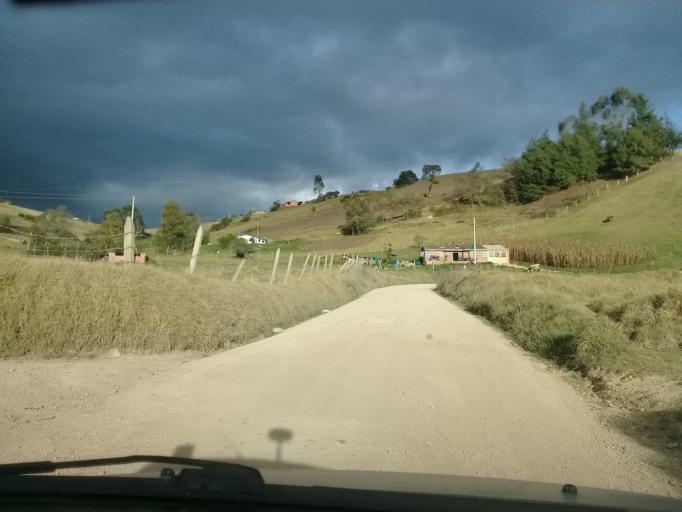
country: CO
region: Cundinamarca
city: Villapinzon
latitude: 5.2138
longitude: -73.6314
